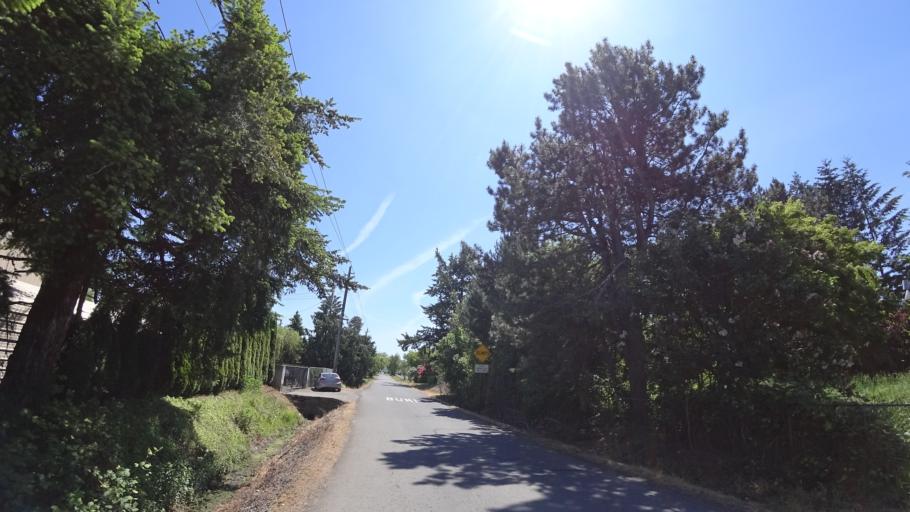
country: US
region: Oregon
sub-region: Clackamas County
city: Happy Valley
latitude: 45.4645
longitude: -122.4876
